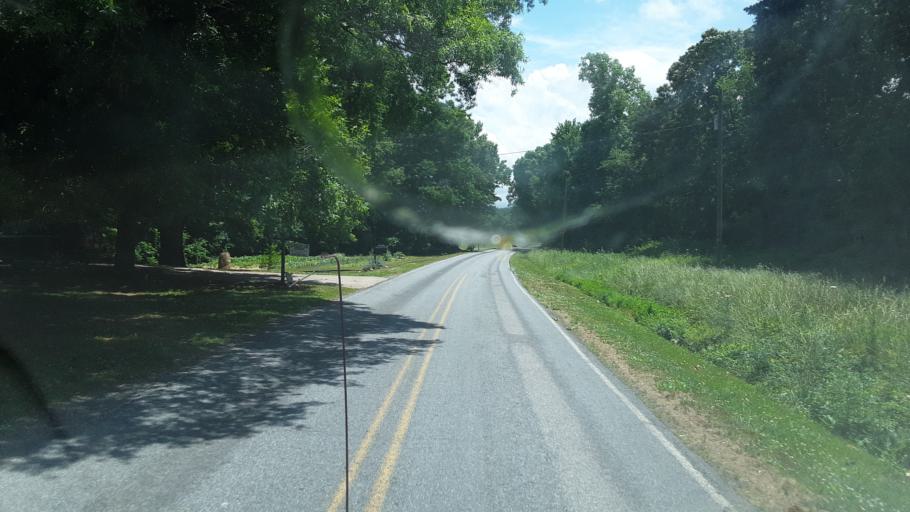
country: US
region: North Carolina
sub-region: Yadkin County
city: Jonesville
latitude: 36.0842
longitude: -80.8614
